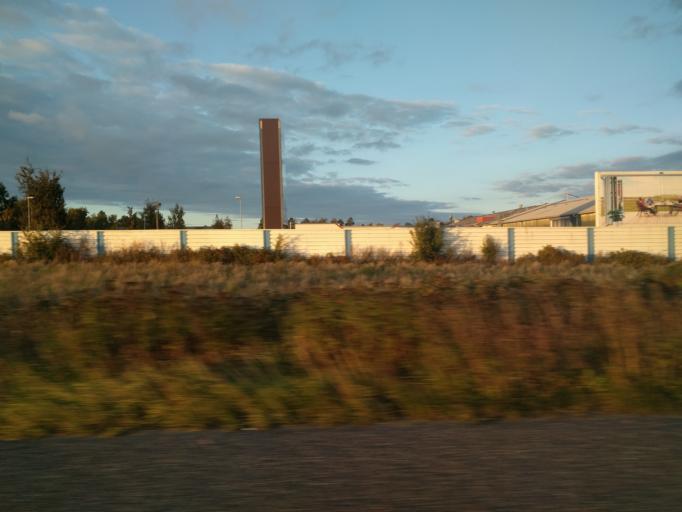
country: DK
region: South Denmark
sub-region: Nyborg Kommune
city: Ullerslev
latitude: 55.3528
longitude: 10.6197
